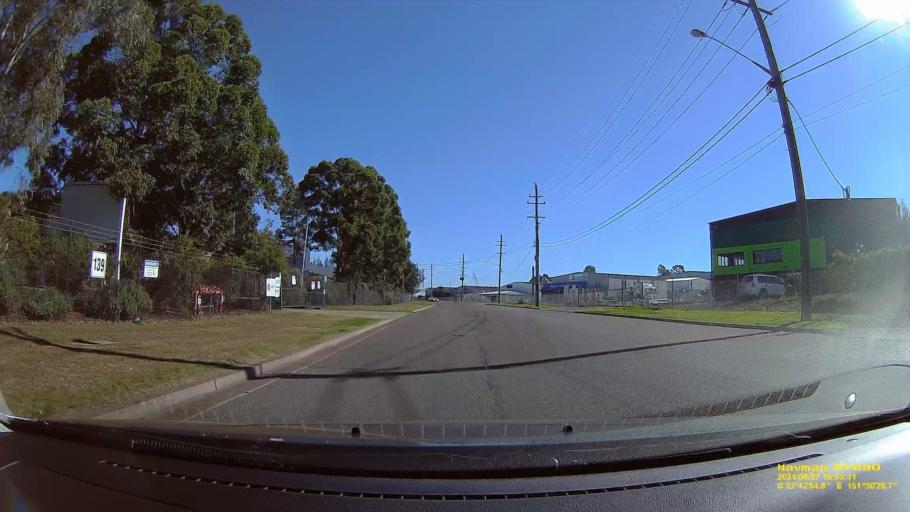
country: AU
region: New South Wales
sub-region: Maitland Municipality
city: Rutherford
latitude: -32.7151
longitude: 151.5079
